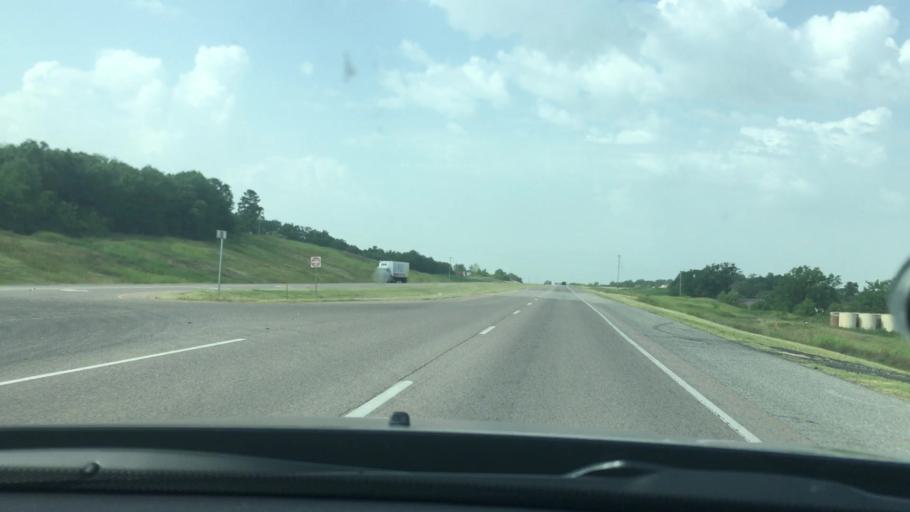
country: US
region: Oklahoma
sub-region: Pontotoc County
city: Byng
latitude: 34.8399
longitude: -96.6870
